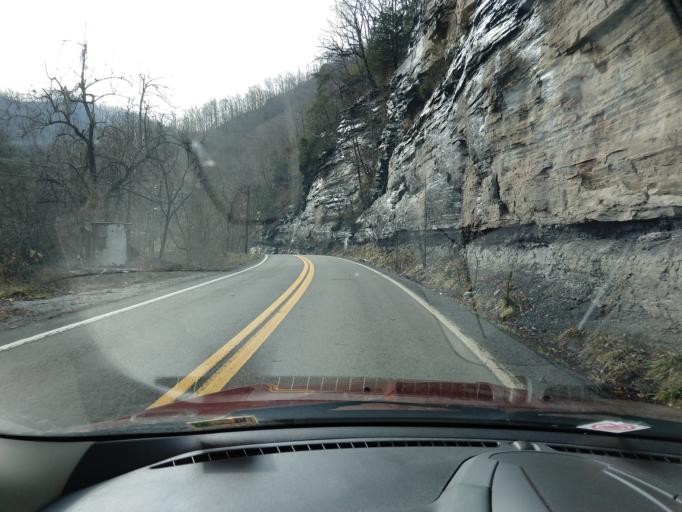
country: US
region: West Virginia
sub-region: McDowell County
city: Welch
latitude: 37.3626
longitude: -81.8013
